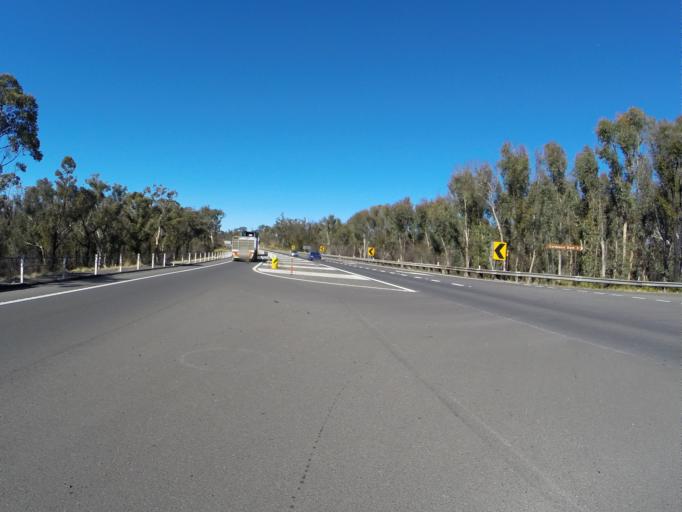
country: AU
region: New South Wales
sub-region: Wollondilly
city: Douglas Park
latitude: -34.3085
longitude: 150.7390
